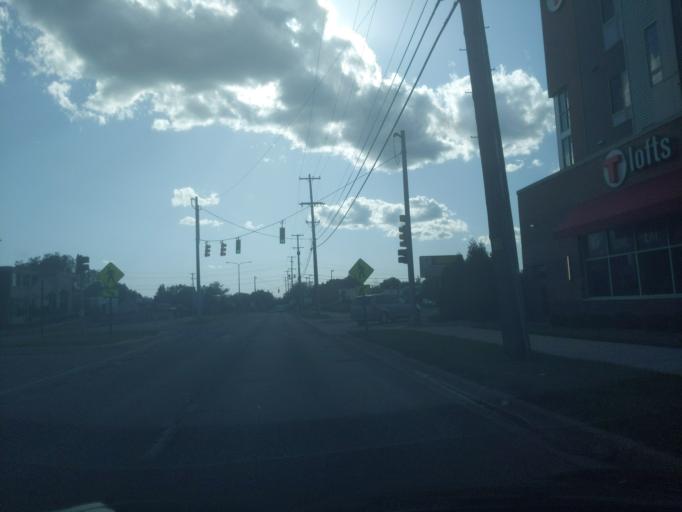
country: US
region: Michigan
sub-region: Ingham County
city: East Lansing
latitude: 42.7199
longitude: -84.4957
